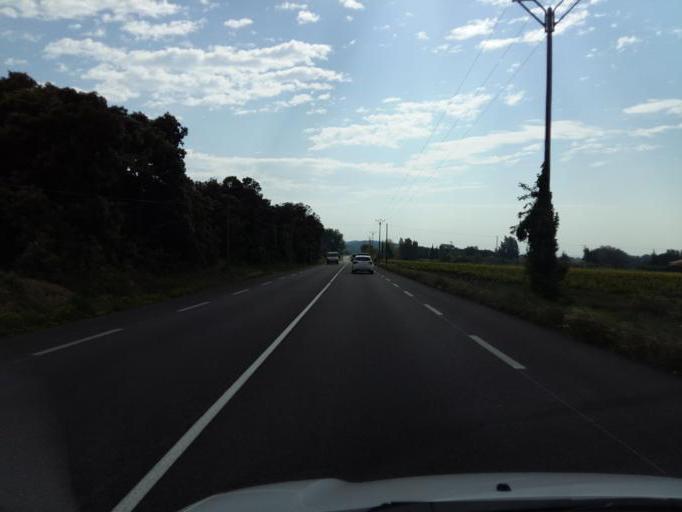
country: FR
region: Rhone-Alpes
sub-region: Departement de la Drome
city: Suze-la-Rousse
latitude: 44.2850
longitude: 4.8145
